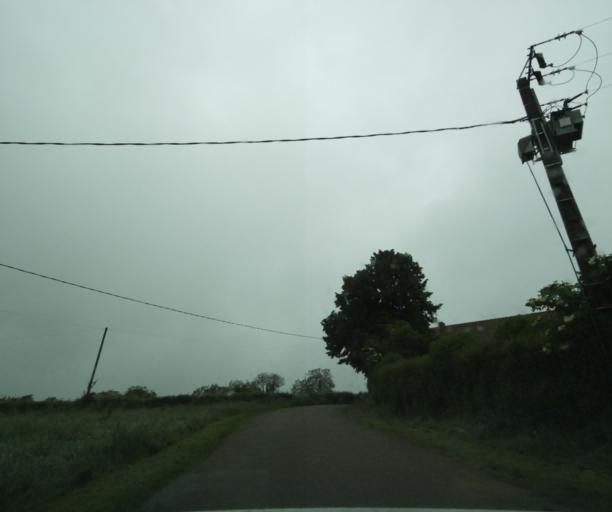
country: FR
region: Bourgogne
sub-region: Departement de Saone-et-Loire
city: Charolles
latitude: 46.4094
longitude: 4.3882
